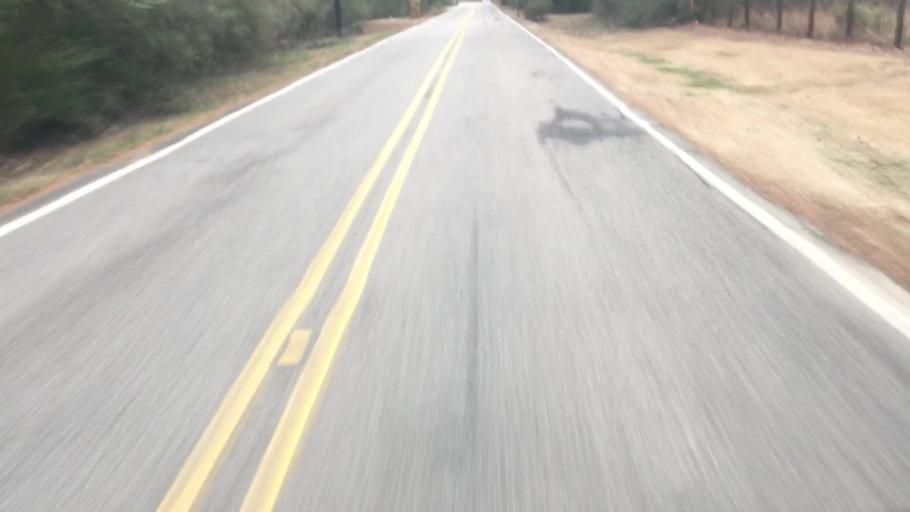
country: US
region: Alabama
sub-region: Jefferson County
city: Cahaba Heights
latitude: 33.4385
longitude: -86.7428
